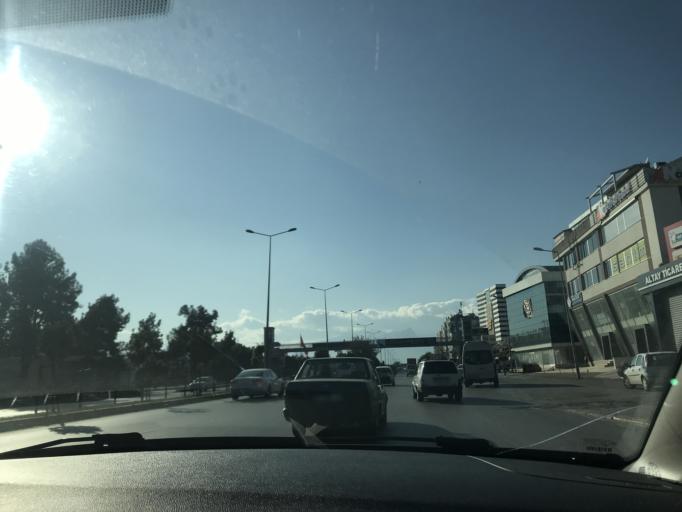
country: TR
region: Antalya
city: Antalya
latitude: 36.9095
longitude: 30.6942
